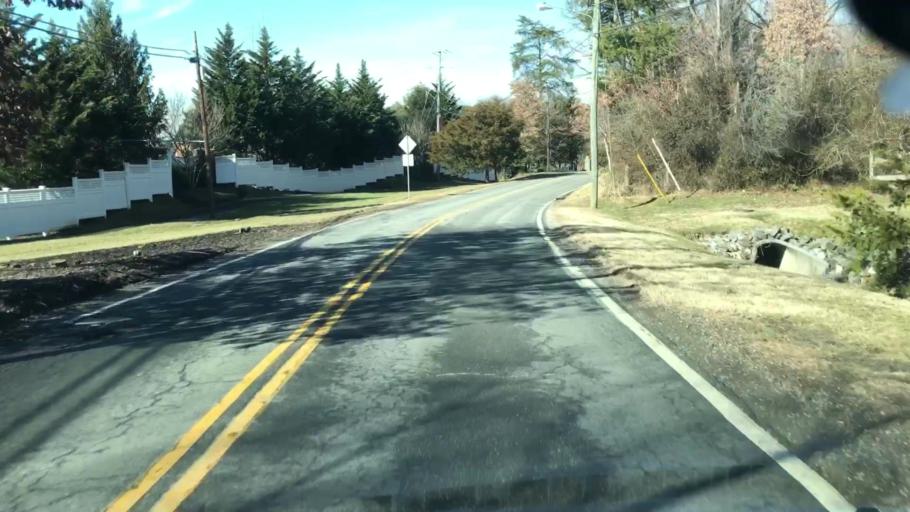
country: US
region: Virginia
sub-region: Fairfax County
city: Oakton
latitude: 38.8699
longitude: -77.3272
